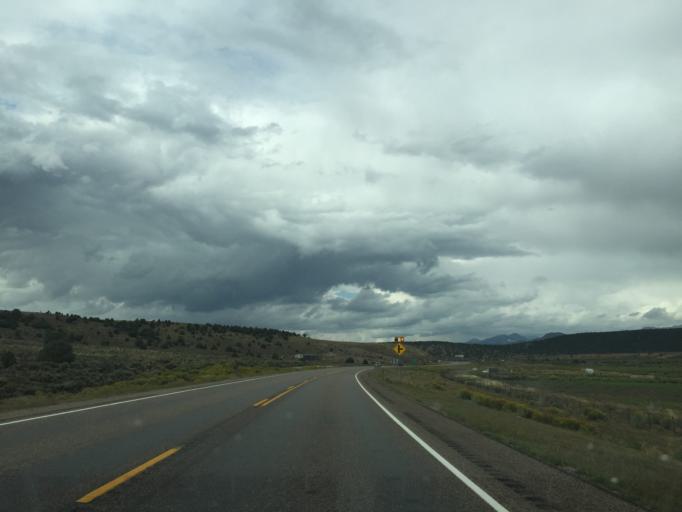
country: US
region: Utah
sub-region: Garfield County
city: Panguitch
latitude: 37.7432
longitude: -112.3797
